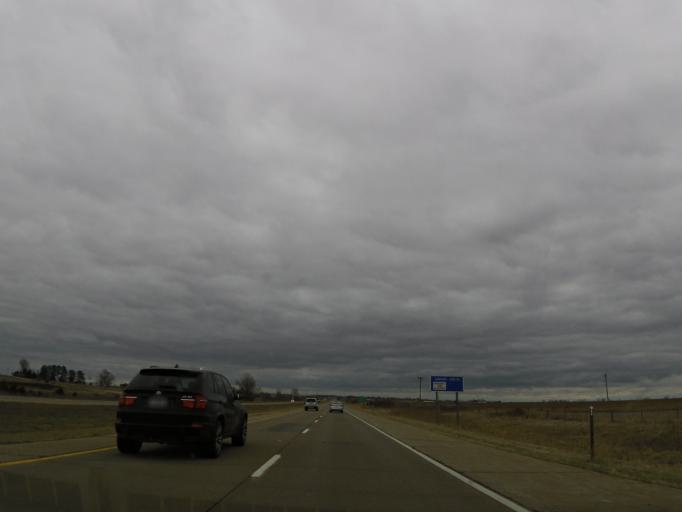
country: US
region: Iowa
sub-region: Benton County
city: Urbana
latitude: 42.2556
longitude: -91.9047
